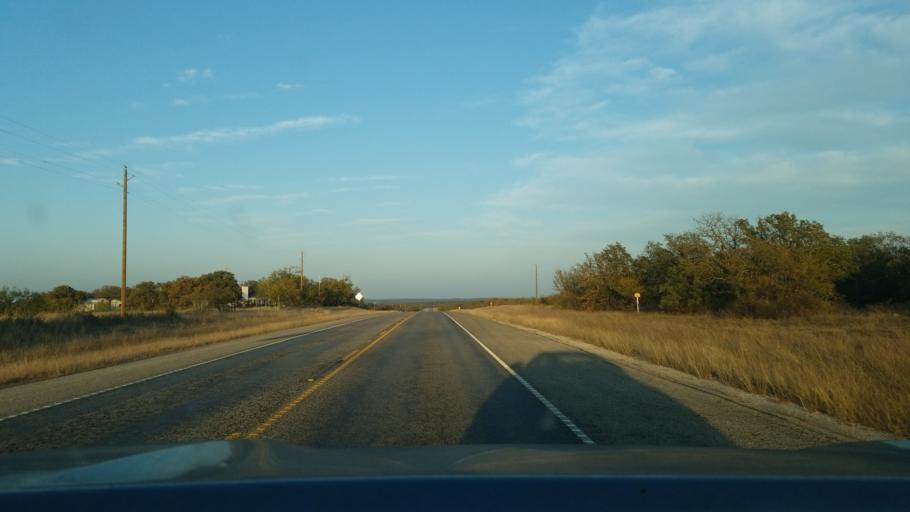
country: US
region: Texas
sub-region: Eastland County
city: Cisco
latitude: 32.3996
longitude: -98.9648
